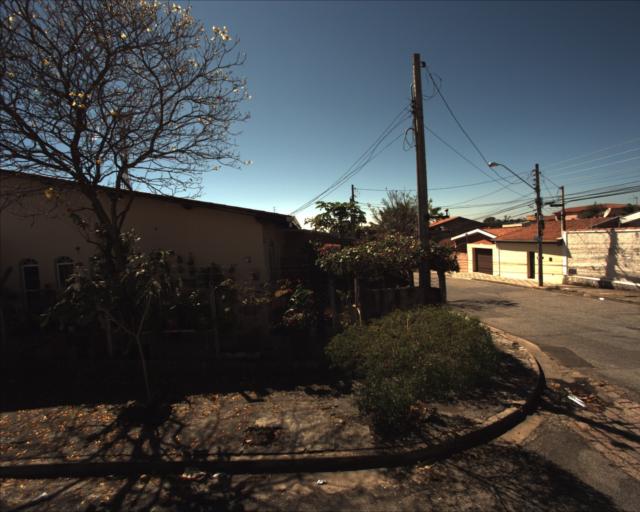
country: BR
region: Sao Paulo
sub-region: Sorocaba
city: Sorocaba
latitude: -23.5057
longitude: -47.4880
